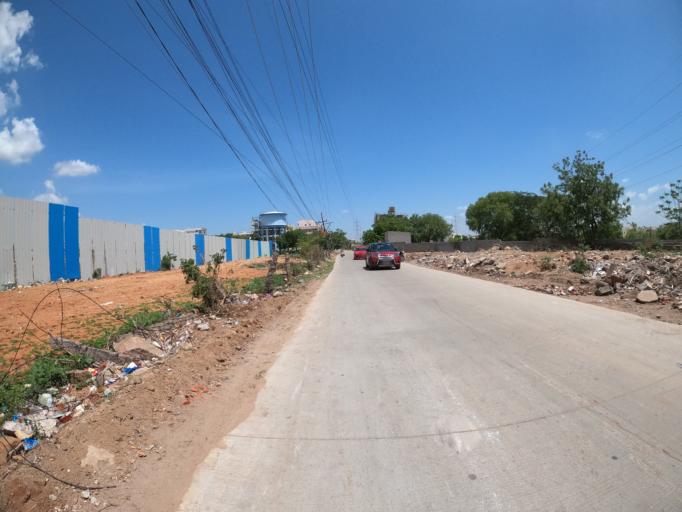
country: IN
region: Telangana
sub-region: Hyderabad
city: Hyderabad
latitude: 17.3575
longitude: 78.3831
